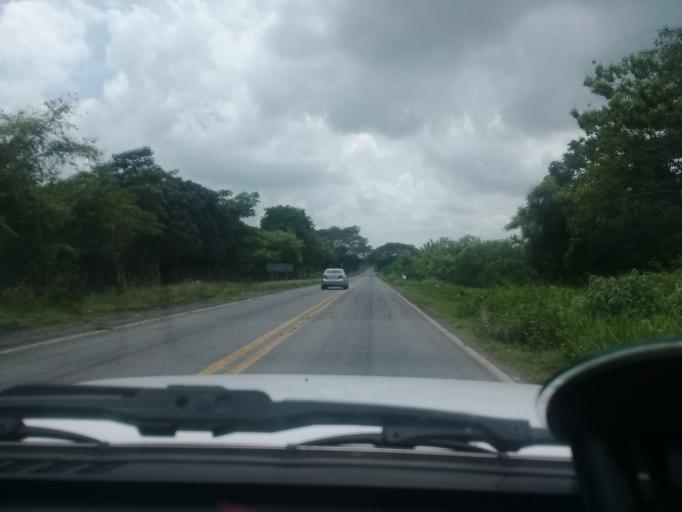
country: MX
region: Veracruz
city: Paso de Ovejas
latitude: 19.2914
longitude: -96.4527
